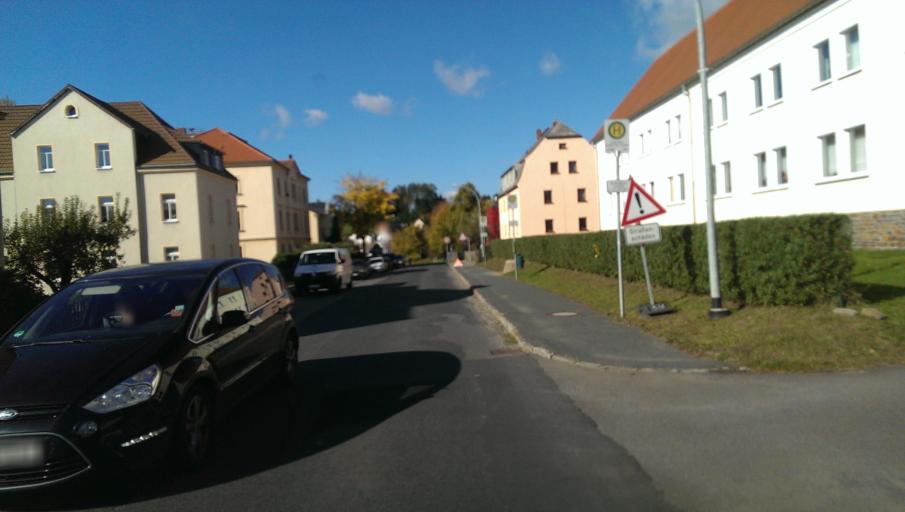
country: DE
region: Saxony
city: Eppendorf
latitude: 50.7988
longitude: 13.2321
